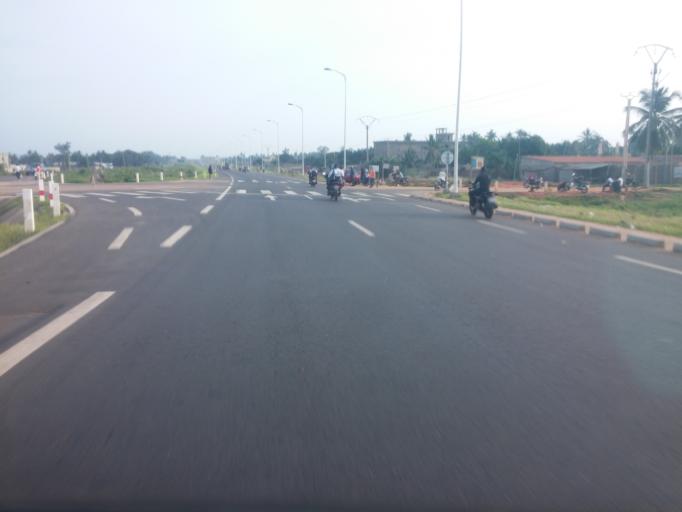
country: TG
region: Maritime
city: Tsevie
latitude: 6.3279
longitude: 1.2187
